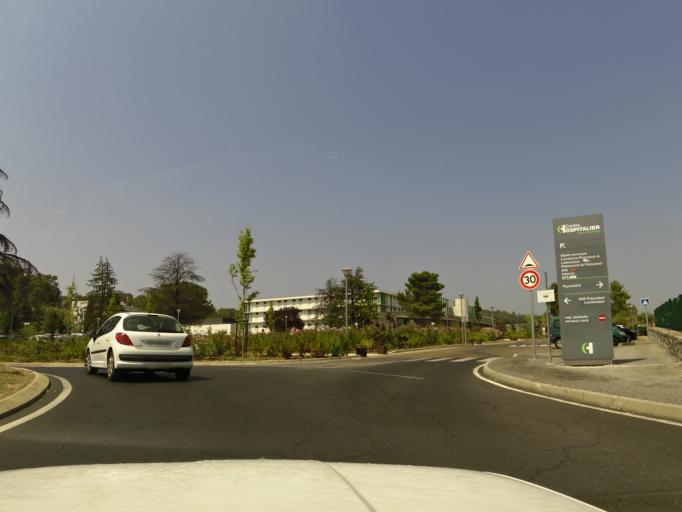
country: FR
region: Languedoc-Roussillon
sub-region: Departement du Gard
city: Ales
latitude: 44.1451
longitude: 4.0960
